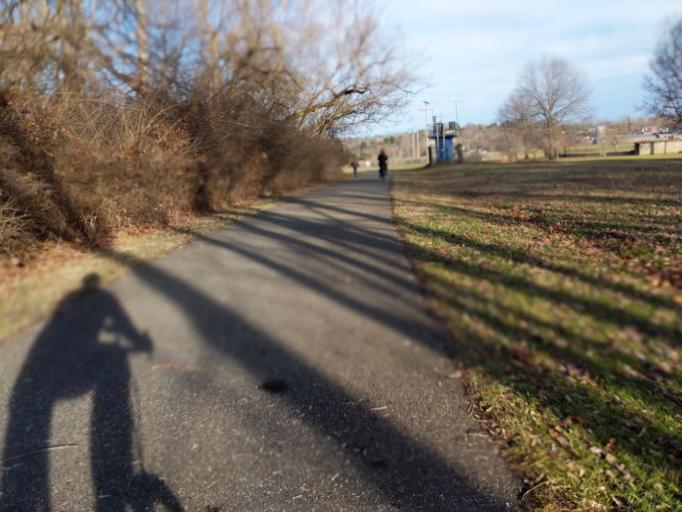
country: US
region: Ohio
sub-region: Athens County
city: Athens
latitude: 39.3363
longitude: -82.1228
